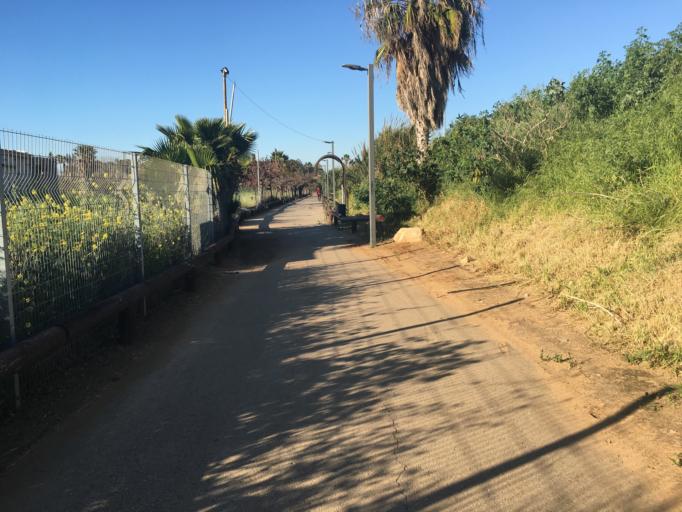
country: IL
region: Tel Aviv
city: Ramat HaSharon
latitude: 32.1460
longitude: 34.8273
